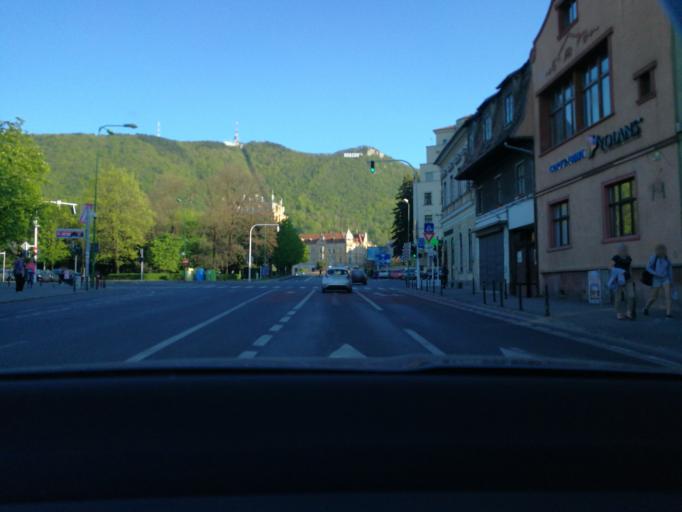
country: RO
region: Brasov
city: Brasov
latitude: 45.6475
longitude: 25.5891
